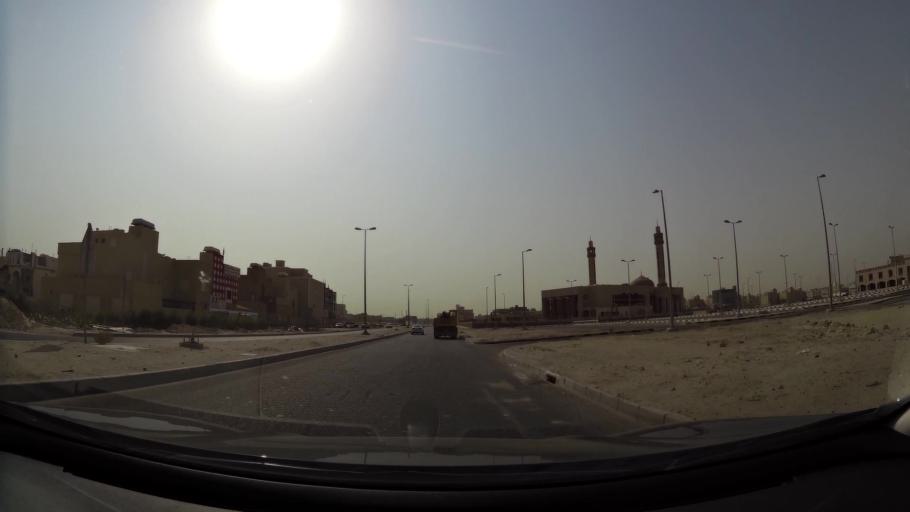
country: KW
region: Muhafazat al Jahra'
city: Al Jahra'
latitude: 29.3538
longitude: 47.7571
